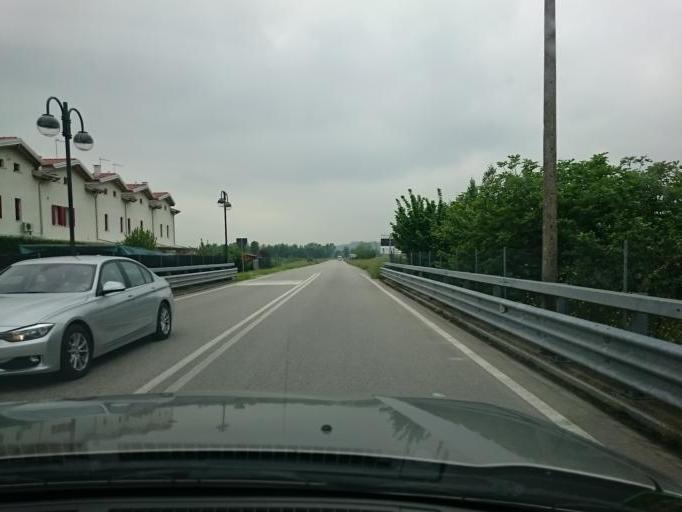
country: IT
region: Veneto
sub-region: Provincia di Padova
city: Terradura
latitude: 45.3241
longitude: 11.8070
